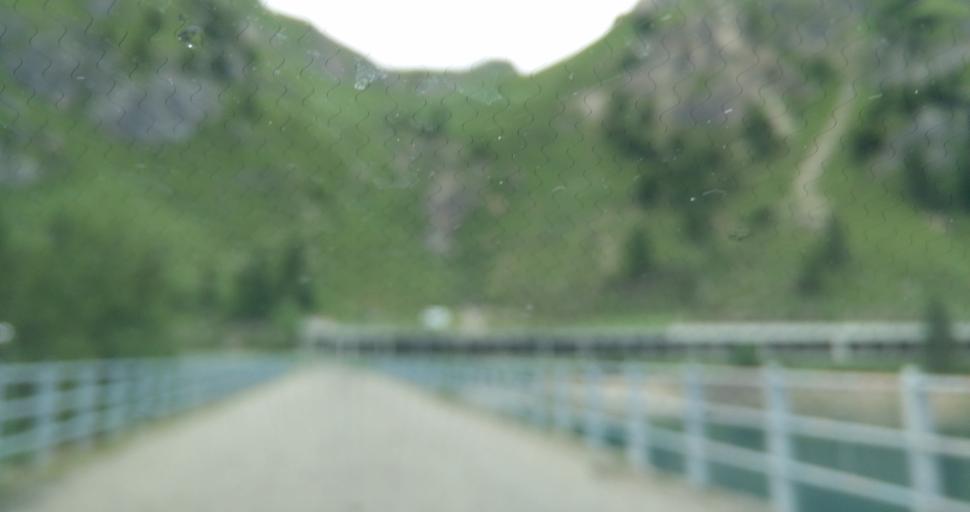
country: IT
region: Trentino-Alto Adige
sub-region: Bolzano
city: Corvara in Badia
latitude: 46.4627
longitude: 11.8626
